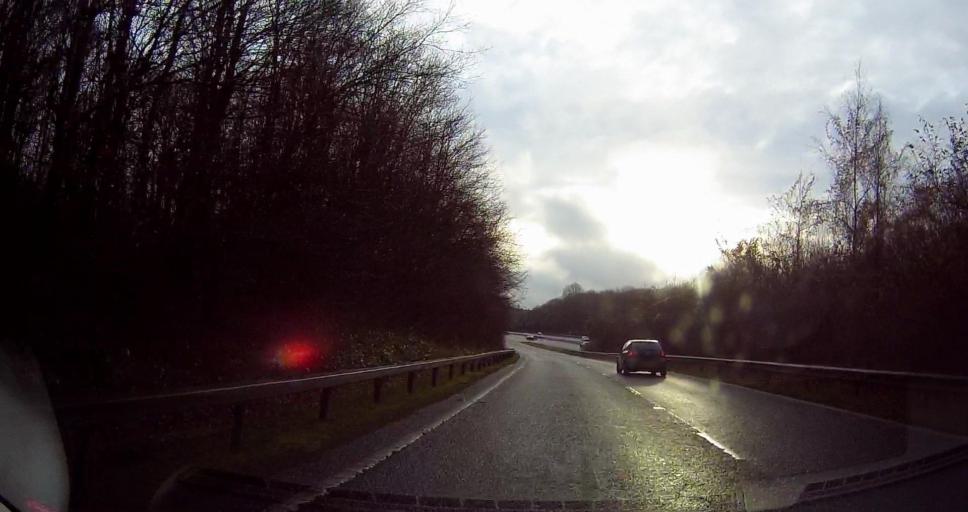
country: GB
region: England
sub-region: Kent
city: Shoreham
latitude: 51.3461
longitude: 0.1574
